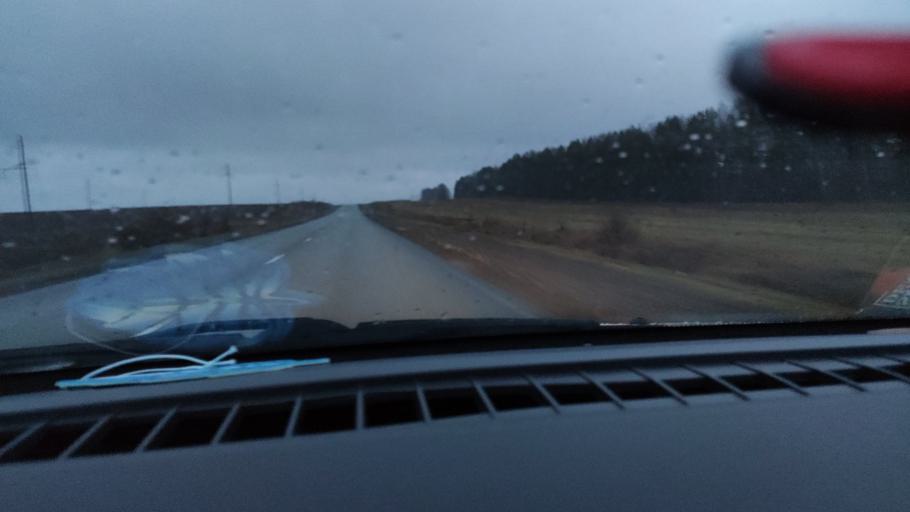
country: RU
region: Udmurtiya
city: Alnashi
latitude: 56.2898
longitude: 52.3531
